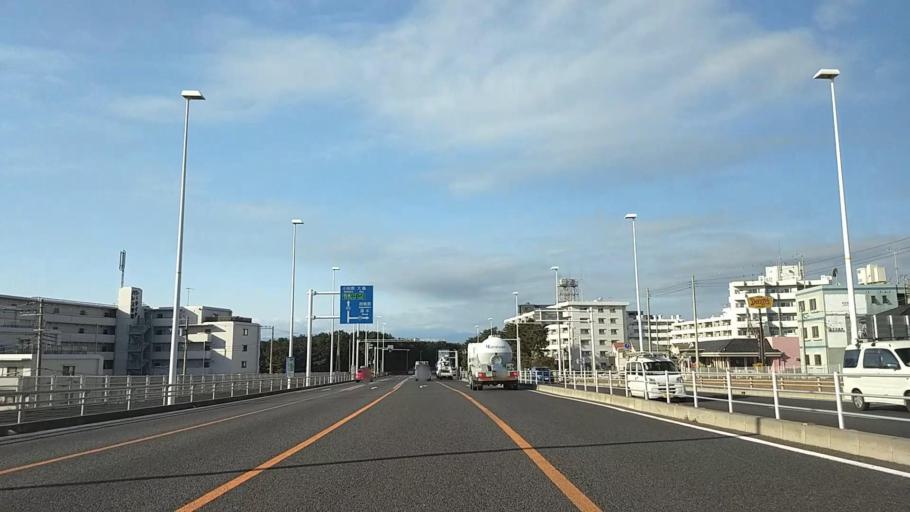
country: JP
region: Kanagawa
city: Hiratsuka
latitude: 35.3171
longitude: 139.3635
